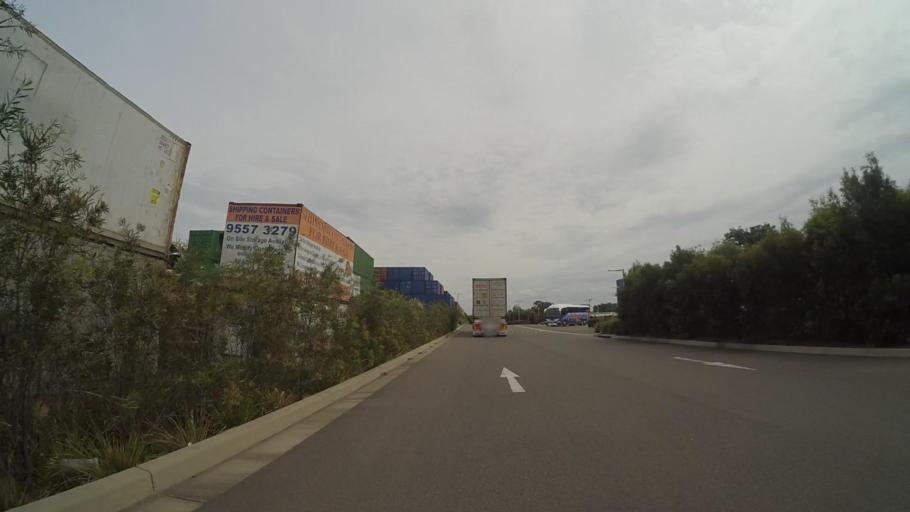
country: AU
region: New South Wales
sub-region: Rockdale
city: Arncliffe
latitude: -33.9233
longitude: 151.1675
